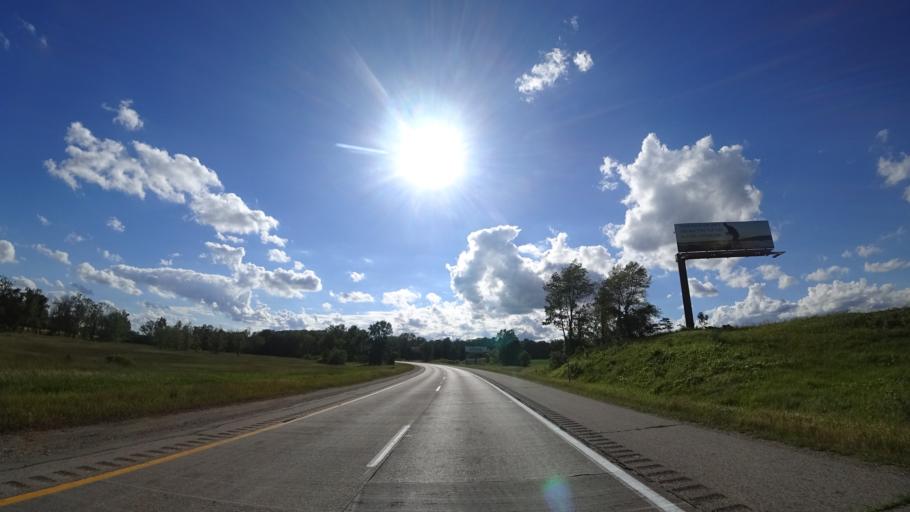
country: US
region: Michigan
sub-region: Ionia County
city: Saranac
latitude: 42.8801
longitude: -85.2790
